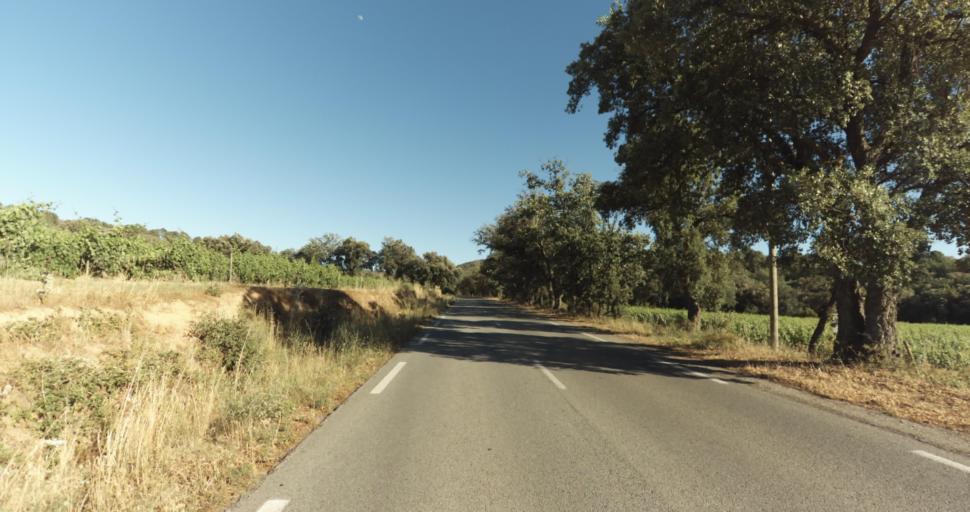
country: FR
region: Provence-Alpes-Cote d'Azur
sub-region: Departement du Var
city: Gassin
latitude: 43.2424
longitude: 6.5969
